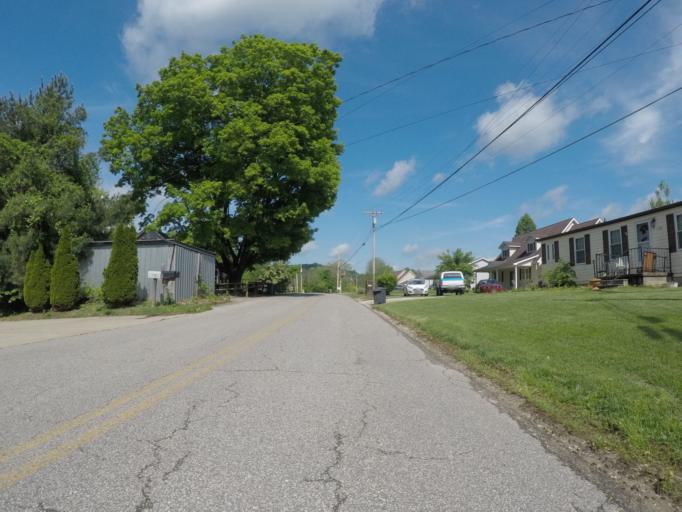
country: US
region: West Virginia
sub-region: Cabell County
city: Huntington
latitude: 38.4480
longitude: -82.4318
